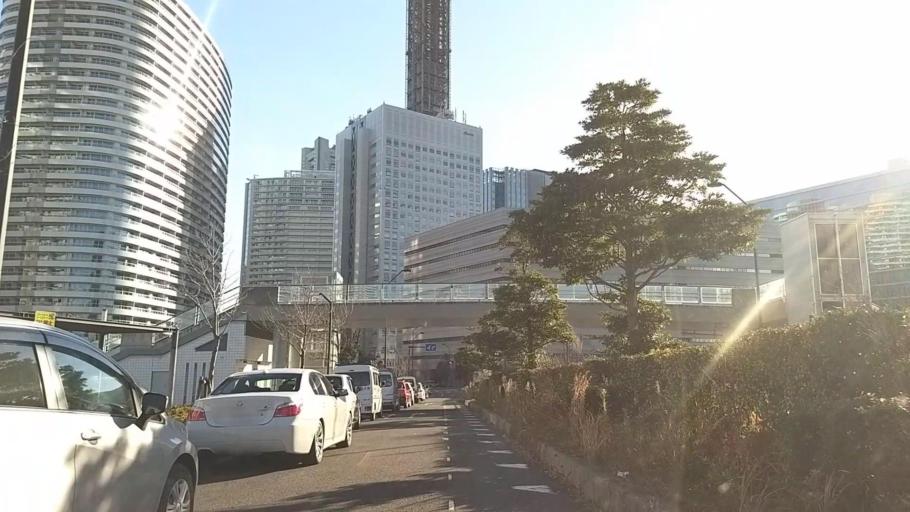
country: JP
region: Kanagawa
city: Yokohama
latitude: 35.4624
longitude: 139.6299
